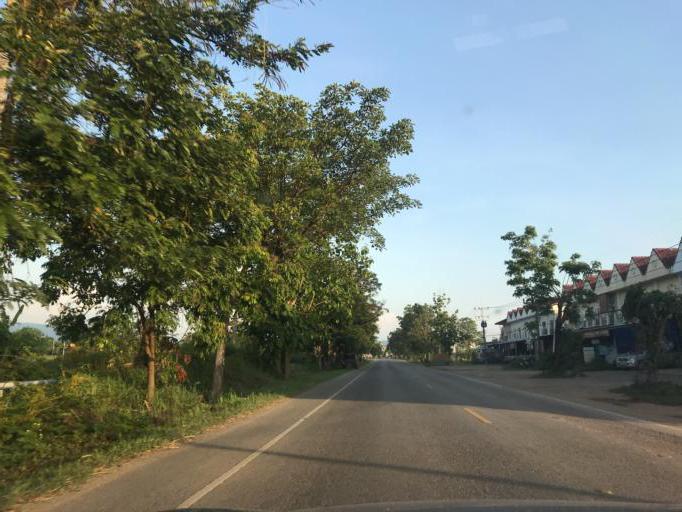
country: TH
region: Phayao
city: Chiang Kham
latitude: 19.5288
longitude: 100.2935
